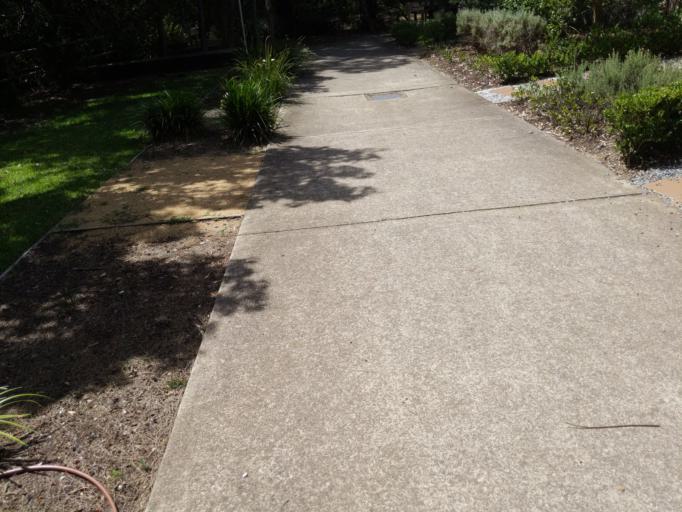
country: AU
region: New South Wales
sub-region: Canada Bay
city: Concord
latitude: -33.8421
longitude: 151.1042
